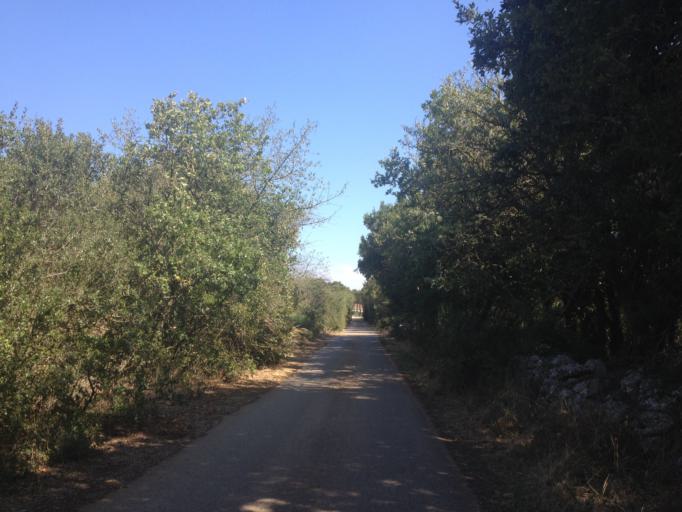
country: IT
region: Apulia
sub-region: Provincia di Bari
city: Sammichele di Bari
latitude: 40.8231
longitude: 17.0130
